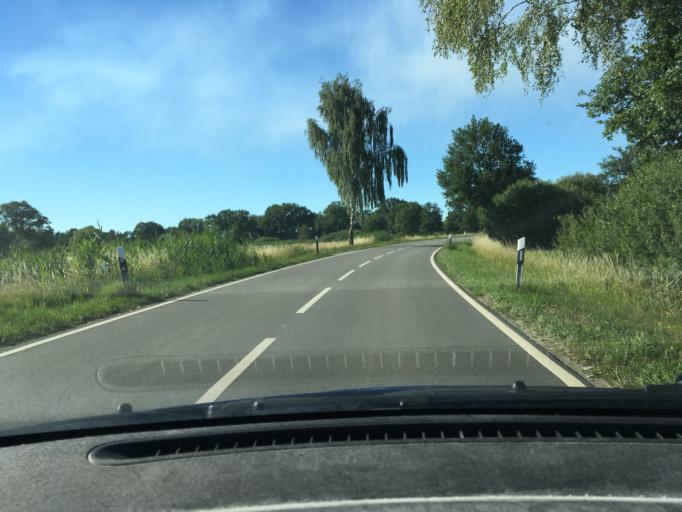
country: DE
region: Lower Saxony
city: Bleckede
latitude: 53.3208
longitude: 10.6748
